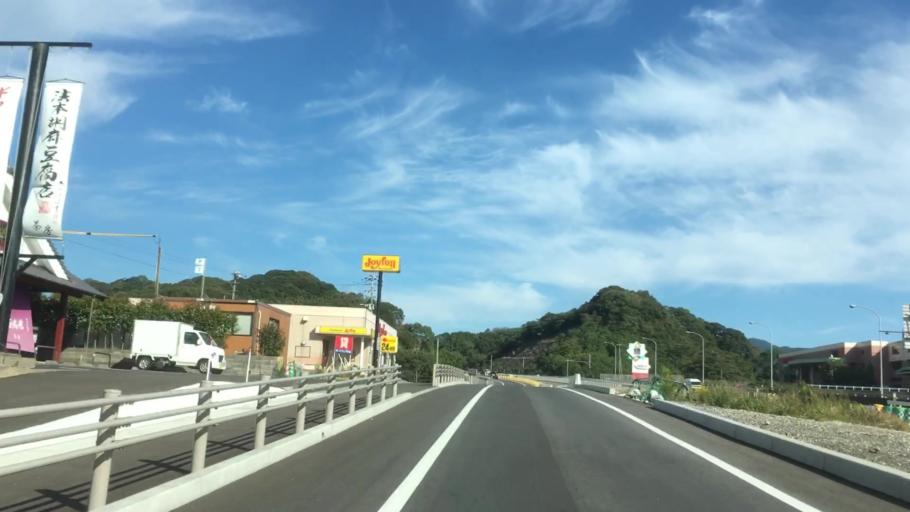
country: JP
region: Nagasaki
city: Sasebo
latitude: 33.1178
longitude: 129.7927
